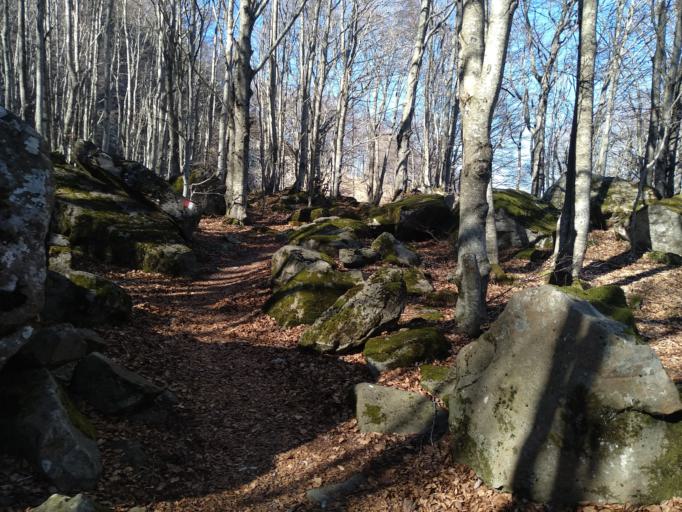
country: IT
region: Emilia-Romagna
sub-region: Provincia di Reggio Emilia
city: Busana
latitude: 44.3796
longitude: 10.2956
